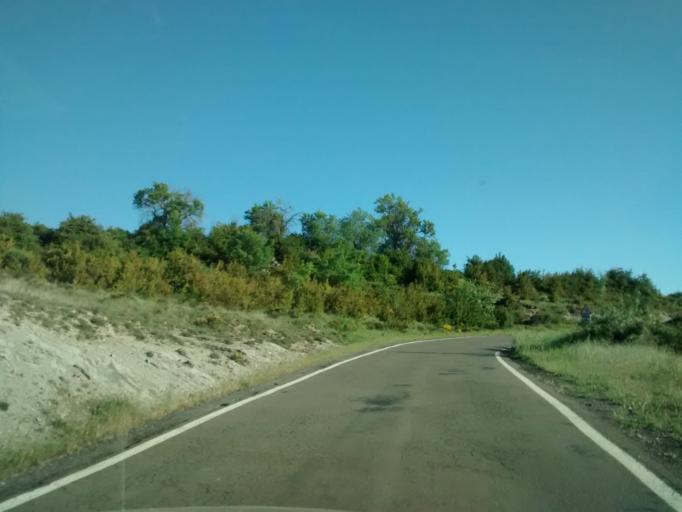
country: ES
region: Aragon
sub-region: Provincia de Huesca
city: Jaca
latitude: 42.5917
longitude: -0.6097
